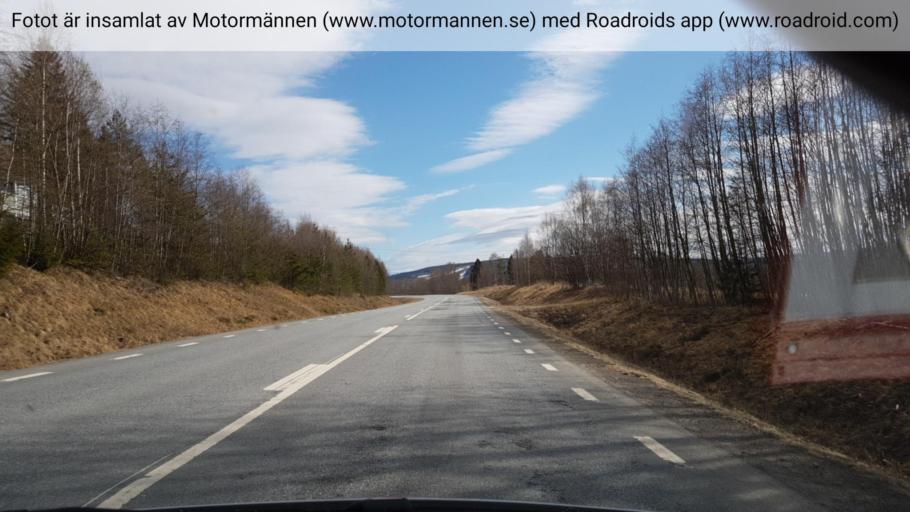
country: SE
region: Vaesternorrland
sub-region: Solleftea Kommun
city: Solleftea
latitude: 63.2003
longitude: 17.2346
